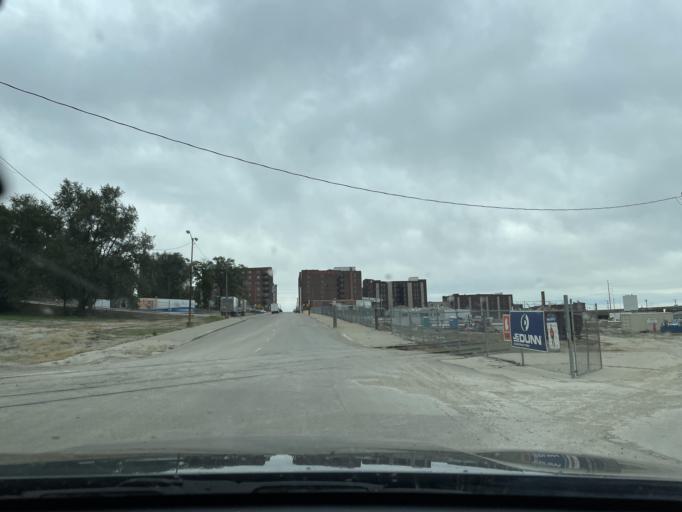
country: US
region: Missouri
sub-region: Buchanan County
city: Saint Joseph
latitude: 39.7721
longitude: -94.8565
